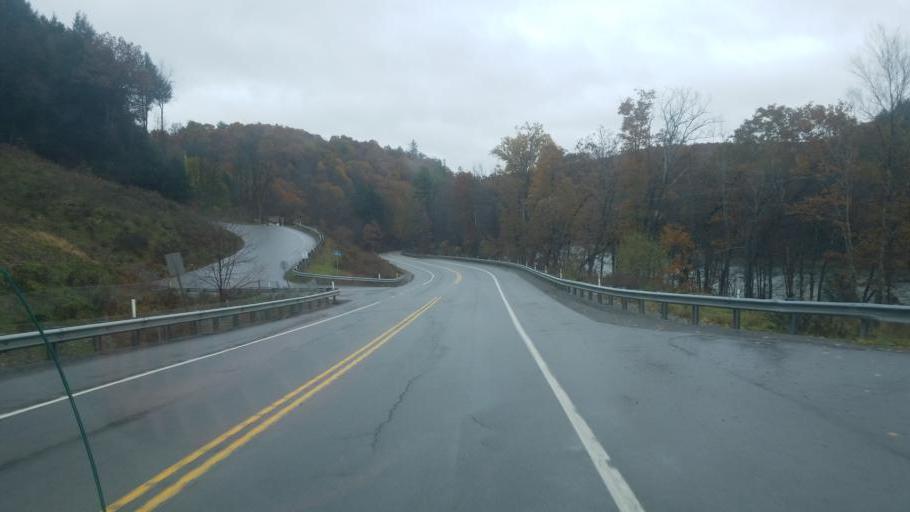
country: US
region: Pennsylvania
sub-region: Clearfield County
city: Clearfield
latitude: 41.0497
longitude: -78.3821
